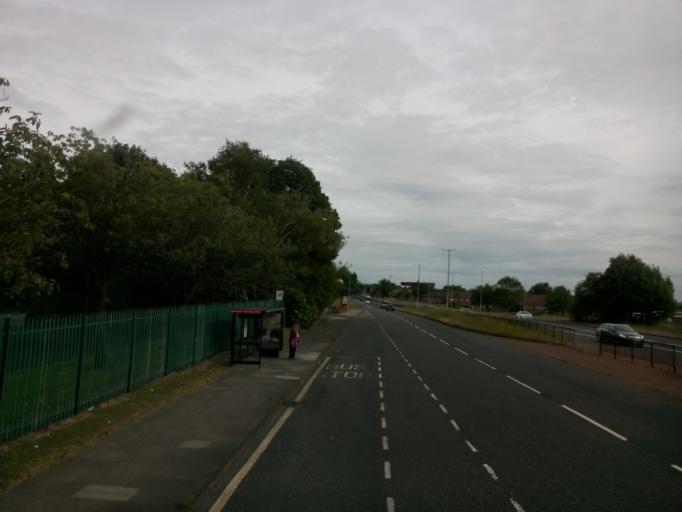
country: GB
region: England
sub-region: Gateshead
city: Lamesley
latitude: 54.9217
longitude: -1.5920
